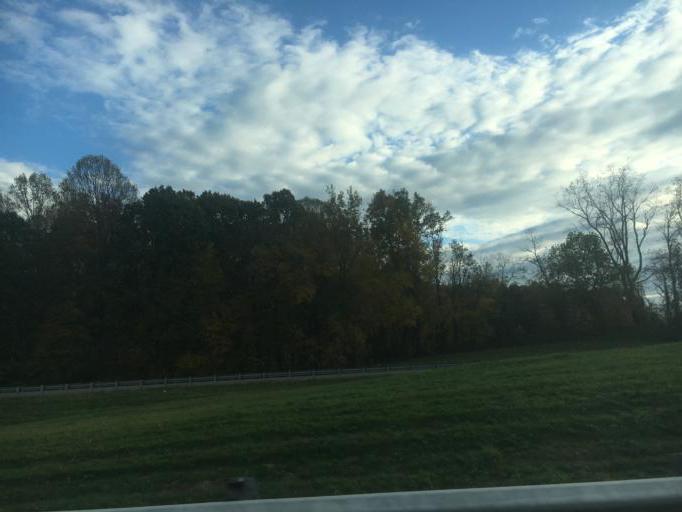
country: US
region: Virginia
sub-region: Washington County
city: Emory
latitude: 36.7686
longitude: -81.8226
